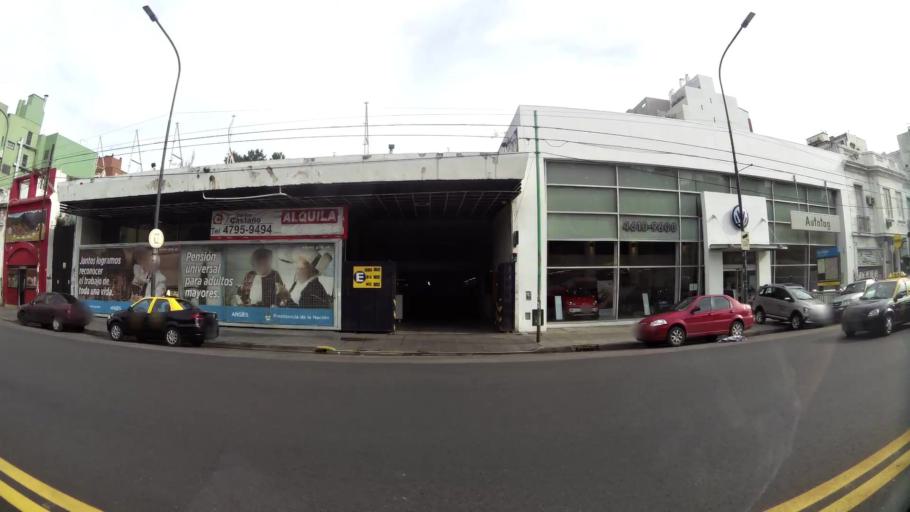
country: AR
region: Buenos Aires F.D.
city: Villa Santa Rita
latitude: -34.6307
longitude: -58.4707
